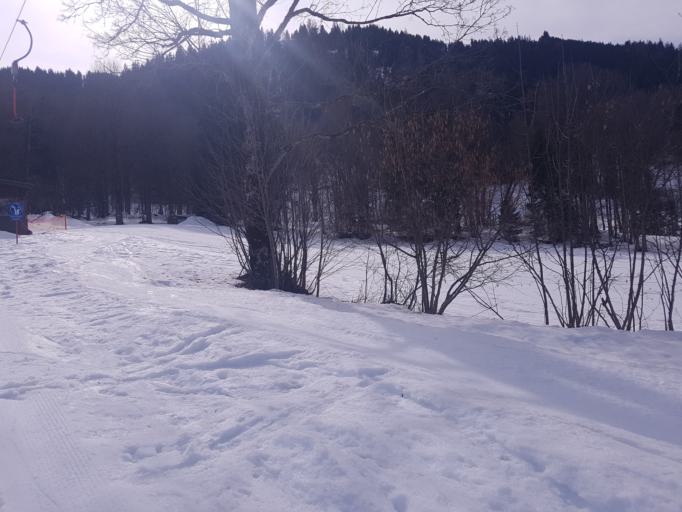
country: AT
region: Tyrol
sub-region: Politischer Bezirk Kufstein
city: Worgl
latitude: 47.4458
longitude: 12.0912
